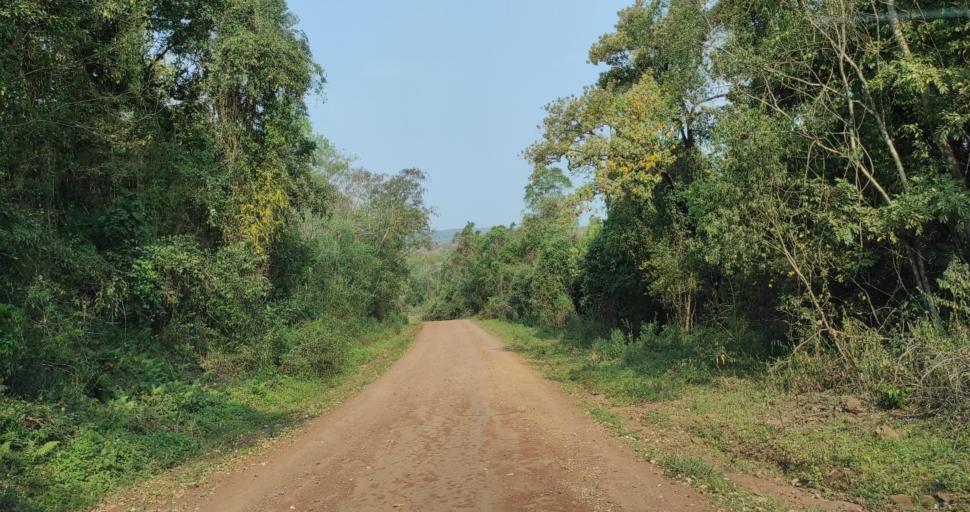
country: AR
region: Misiones
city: Cerro Cora
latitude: -27.5348
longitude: -55.5891
